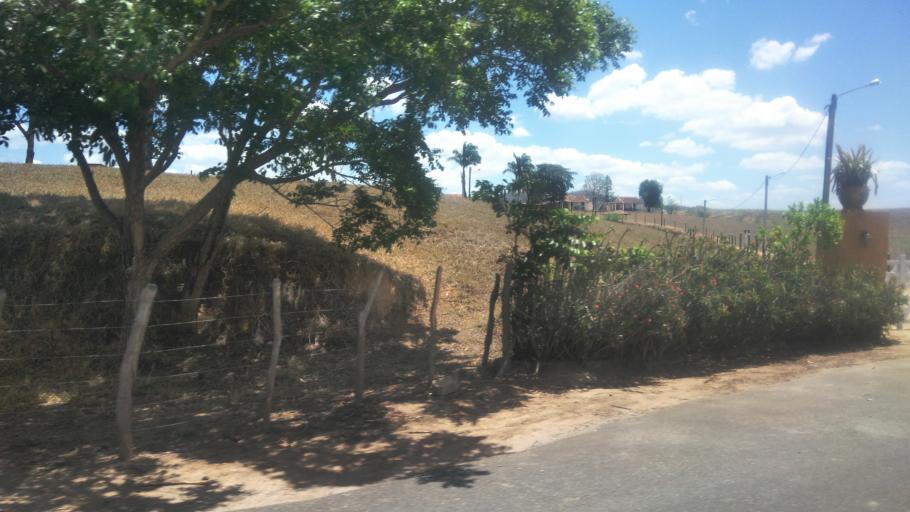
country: BR
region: Pernambuco
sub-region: Nazare Da Mata
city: Nazare da Mata
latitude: -7.7388
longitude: -35.2934
